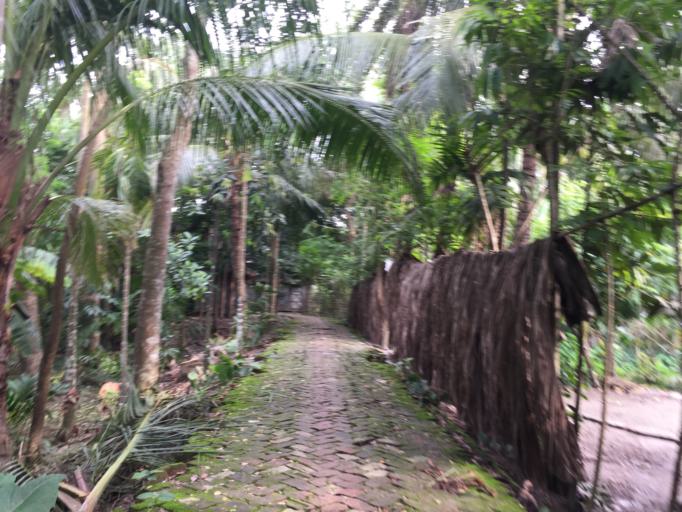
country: BD
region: Barisal
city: Mathba
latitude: 22.1909
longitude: 89.9248
